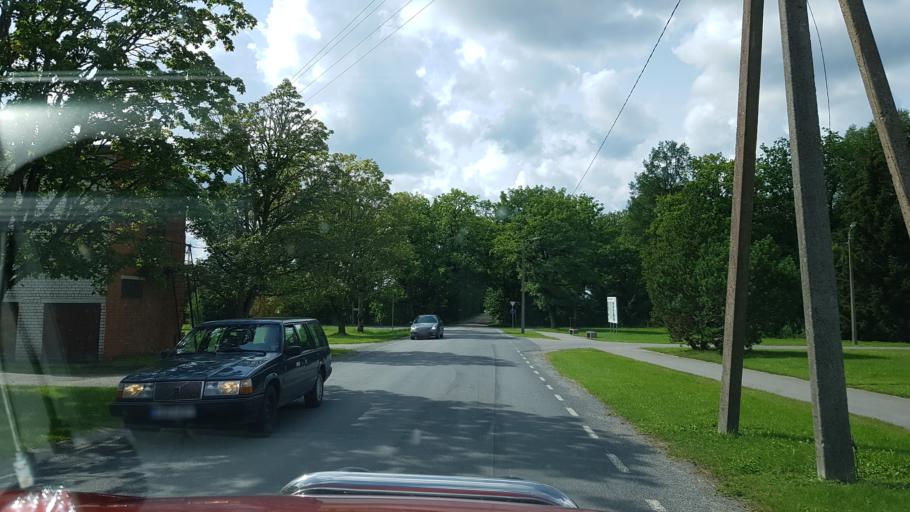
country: EE
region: Raplamaa
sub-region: Maerjamaa vald
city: Marjamaa
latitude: 58.7801
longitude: 24.2488
